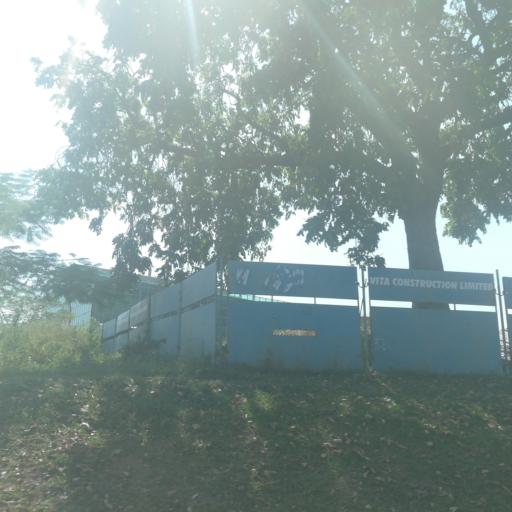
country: NG
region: Abuja Federal Capital Territory
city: Abuja
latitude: 9.0763
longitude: 7.4343
